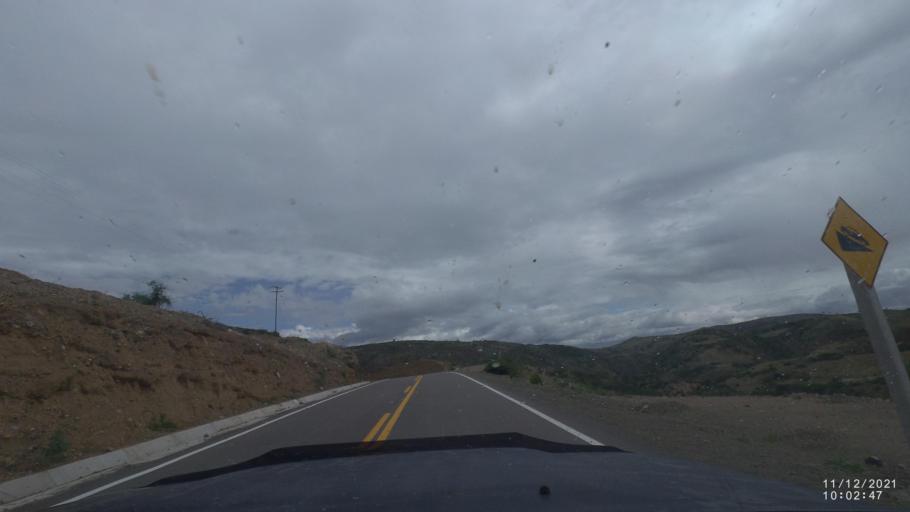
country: BO
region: Cochabamba
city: Cliza
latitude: -17.7193
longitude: -65.9345
